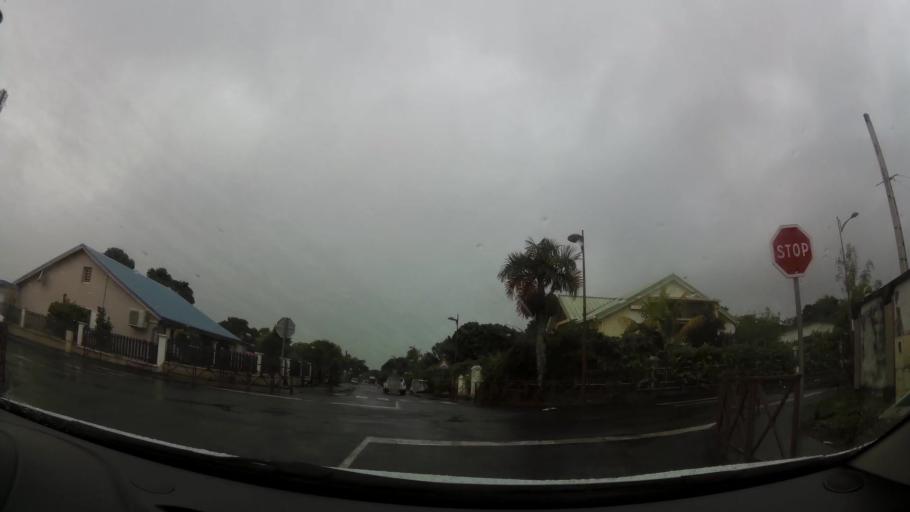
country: RE
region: Reunion
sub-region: Reunion
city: Saint-Andre
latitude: -20.9728
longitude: 55.6575
